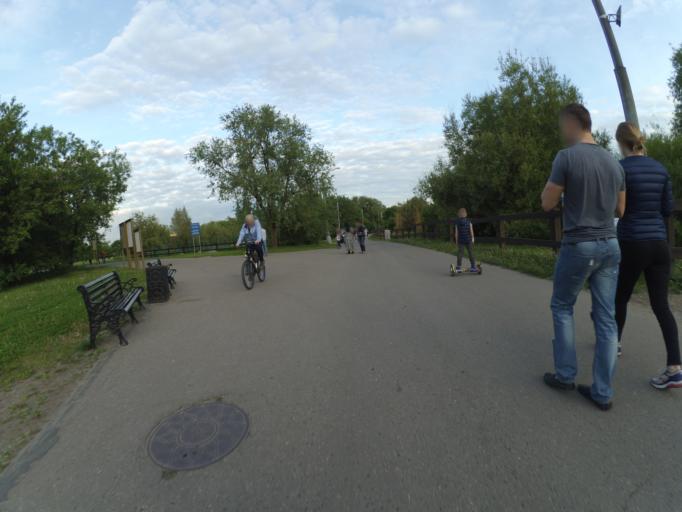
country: RU
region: Moscow
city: Kolomenskoye
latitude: 55.6736
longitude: 37.6785
